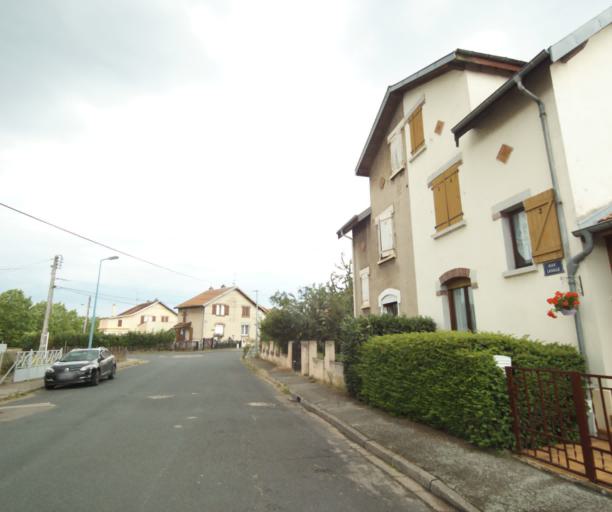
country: FR
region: Lorraine
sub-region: Departement de Meurthe-et-Moselle
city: Chanteheux
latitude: 48.5879
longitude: 6.5176
